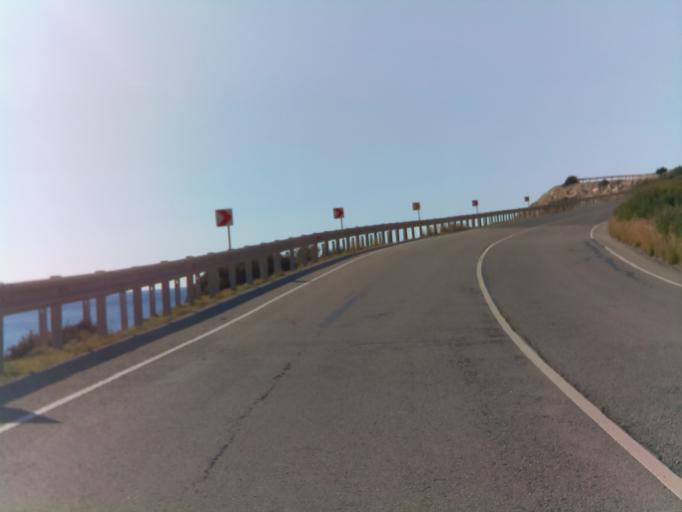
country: CY
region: Limassol
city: Pissouri
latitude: 34.6588
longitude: 32.6497
